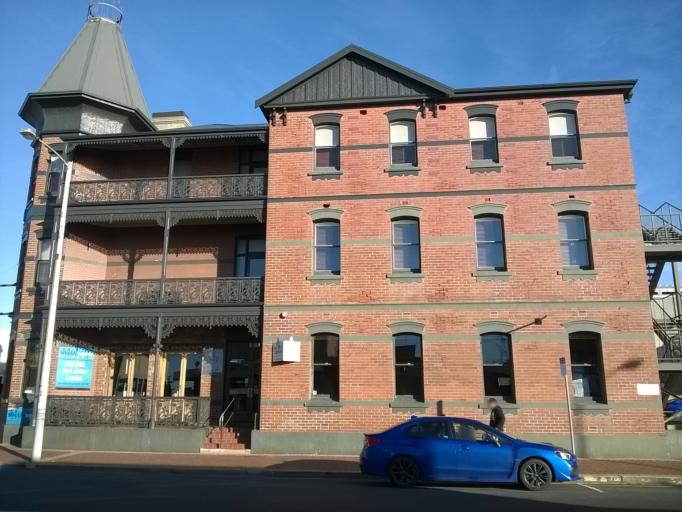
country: AU
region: Tasmania
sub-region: Burnie
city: Burnie
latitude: -41.0507
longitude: 145.9050
